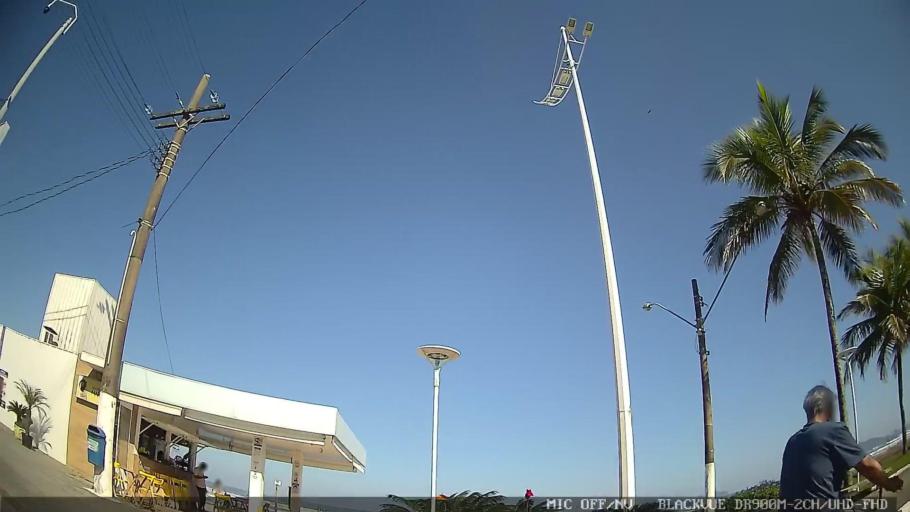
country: BR
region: Sao Paulo
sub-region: Guaruja
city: Guaruja
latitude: -23.9851
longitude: -46.2175
